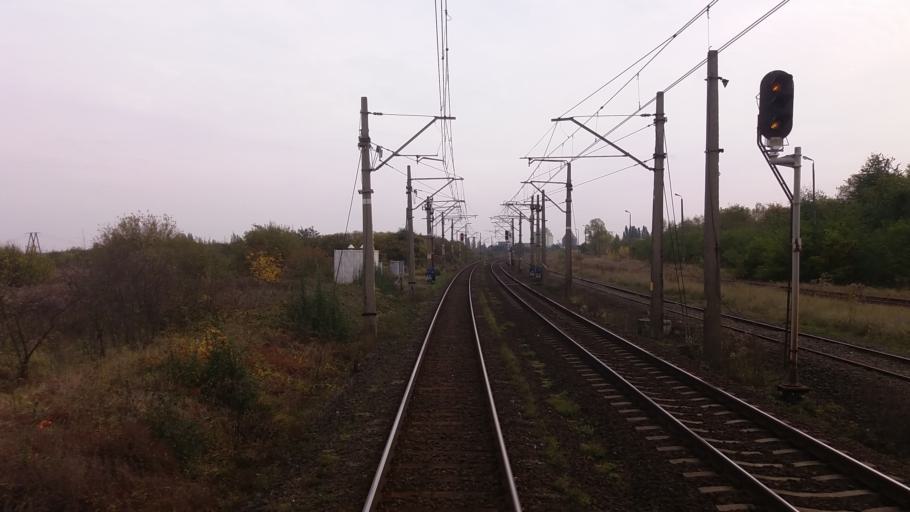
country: PL
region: West Pomeranian Voivodeship
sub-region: Powiat stargardzki
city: Stargard Szczecinski
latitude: 53.3536
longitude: 15.0070
